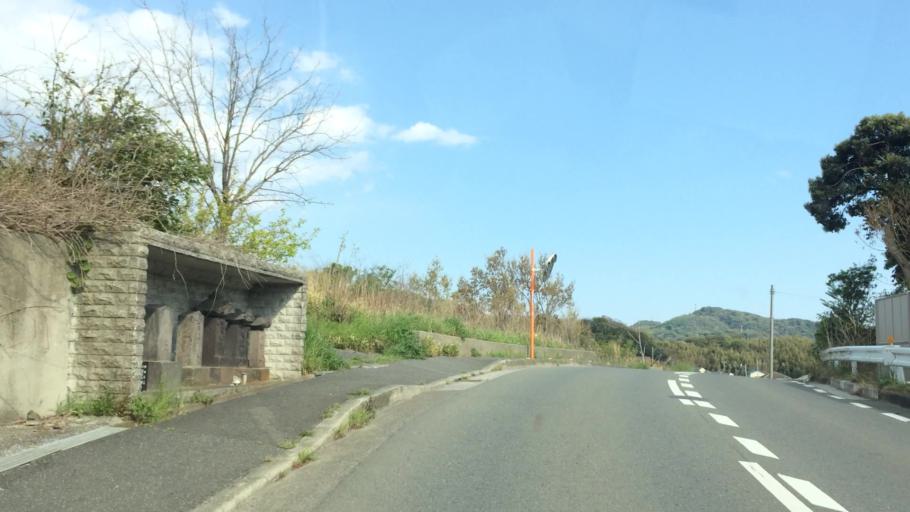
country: JP
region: Kanagawa
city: Yokosuka
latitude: 35.2328
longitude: 139.6288
